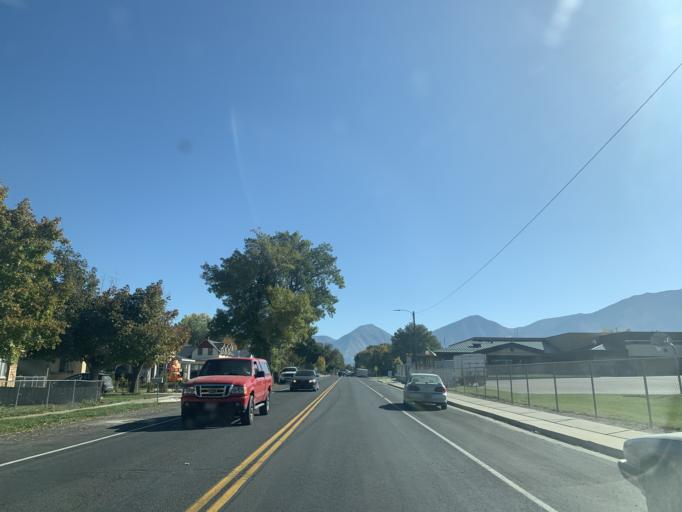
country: US
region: Utah
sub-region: Utah County
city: Payson
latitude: 40.0436
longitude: -111.7417
